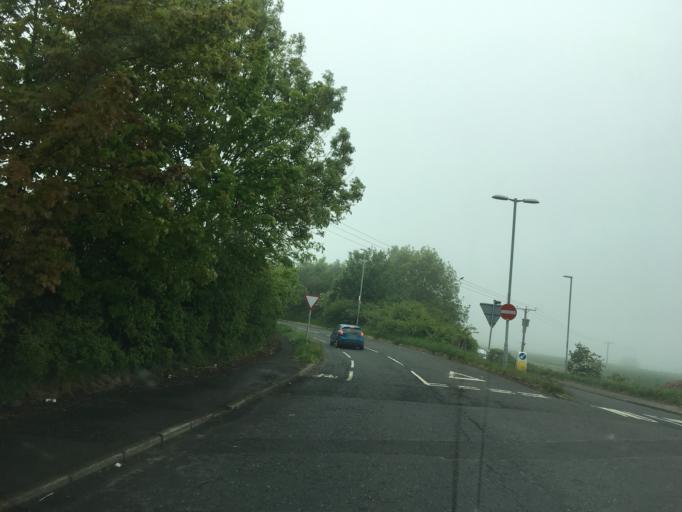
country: GB
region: Scotland
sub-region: Midlothian
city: Penicuik
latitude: 55.8514
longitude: -3.1906
